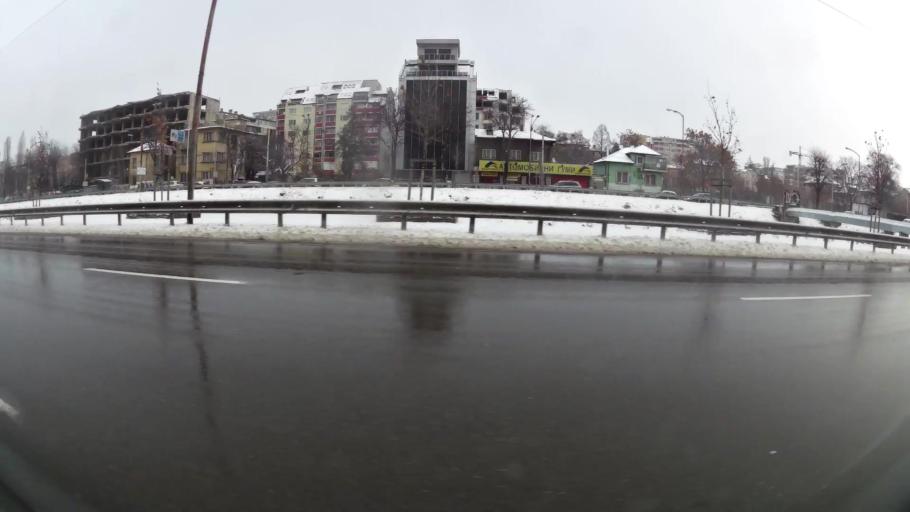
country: BG
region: Sofia-Capital
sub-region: Stolichna Obshtina
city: Sofia
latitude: 42.7055
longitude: 23.3140
